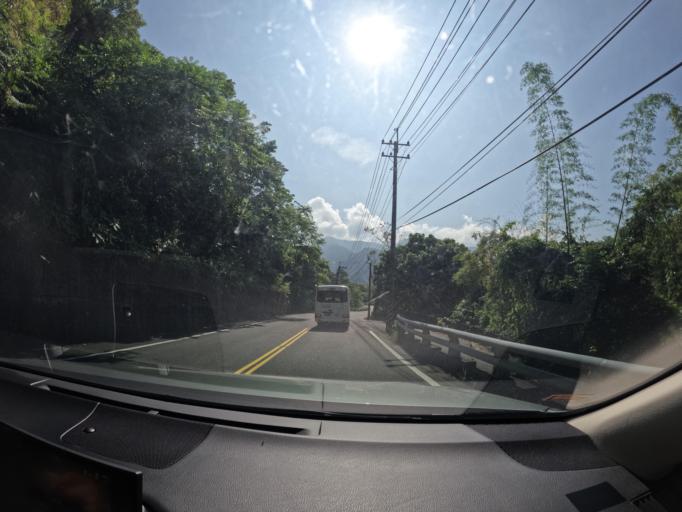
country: TW
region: Taiwan
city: Yujing
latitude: 23.0711
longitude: 120.6608
